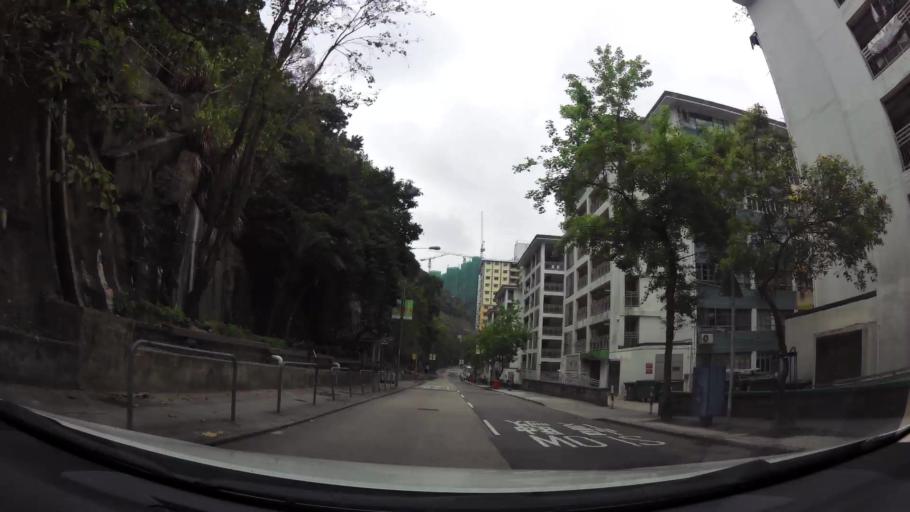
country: HK
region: Wanchai
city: Wan Chai
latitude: 22.2791
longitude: 114.2313
